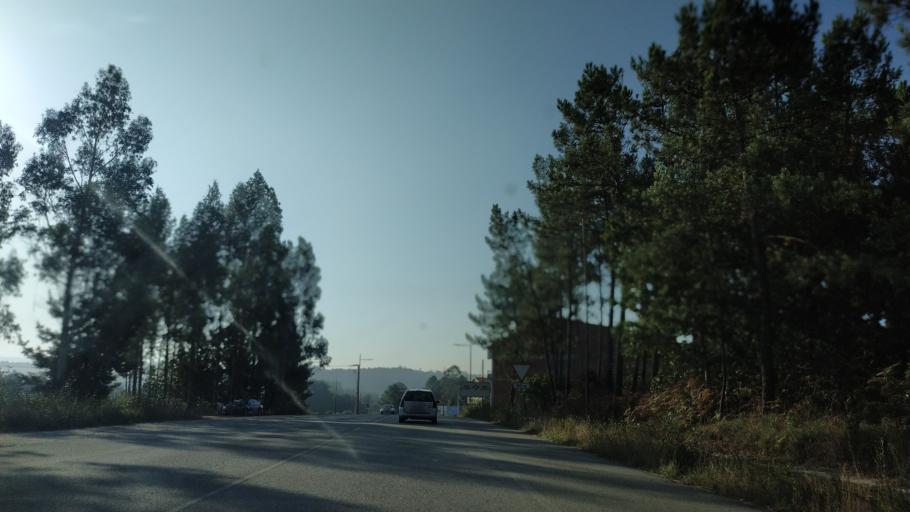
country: ES
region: Galicia
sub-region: Provincia da Coruna
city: Carballo
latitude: 43.2297
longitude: -8.6772
